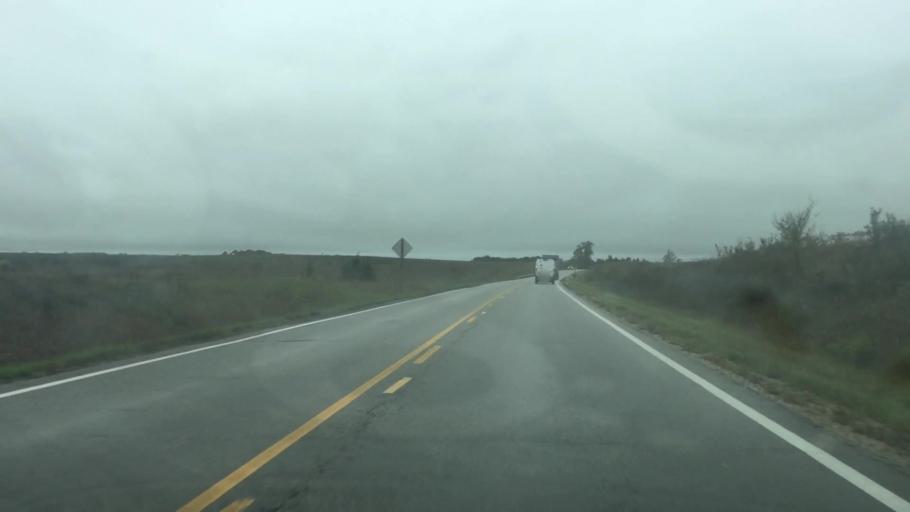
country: US
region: Kansas
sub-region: Anderson County
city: Garnett
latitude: 38.1824
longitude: -95.2623
